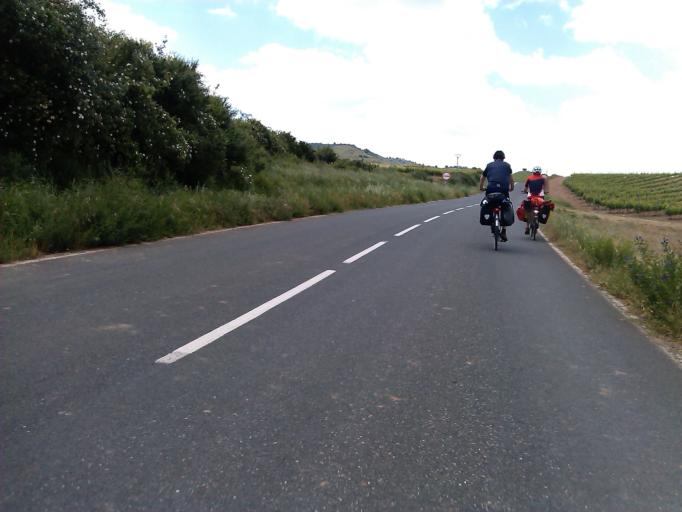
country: ES
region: La Rioja
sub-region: Provincia de La Rioja
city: Ventosa
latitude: 42.3997
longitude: -2.6072
